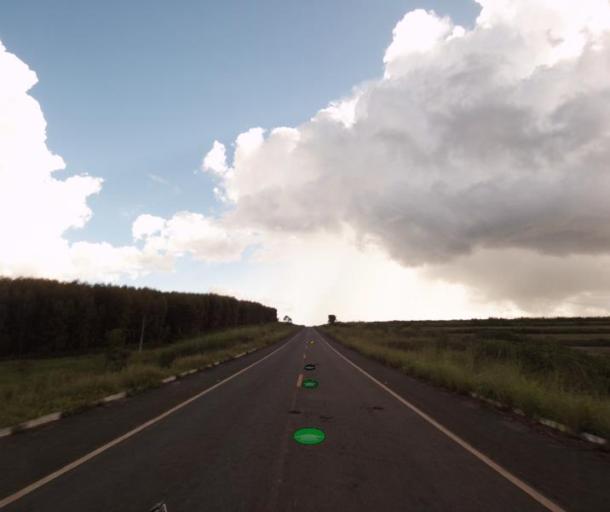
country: BR
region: Goias
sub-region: Itaberai
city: Itaberai
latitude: -15.9880
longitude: -49.7149
